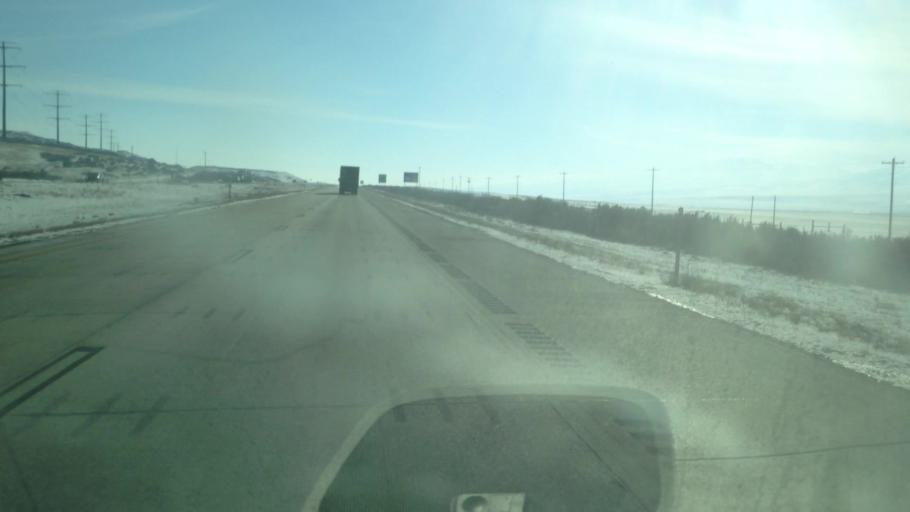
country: US
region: Utah
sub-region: Box Elder County
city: Garland
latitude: 41.9093
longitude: -112.1714
